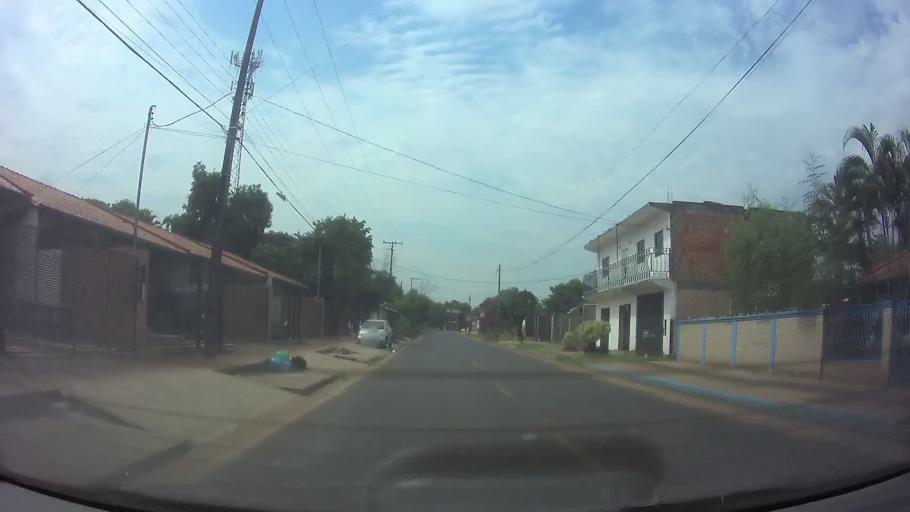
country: PY
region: Central
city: San Lorenzo
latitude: -25.2964
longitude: -57.5112
